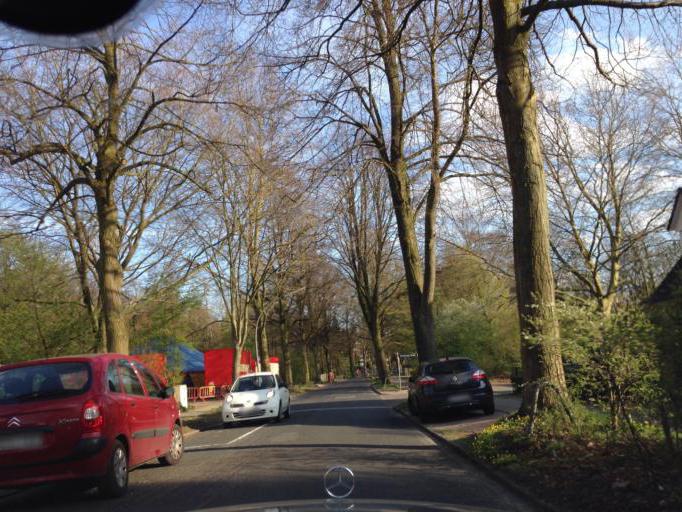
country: DE
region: Hamburg
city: Wandsbek
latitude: 53.5869
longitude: 10.1086
